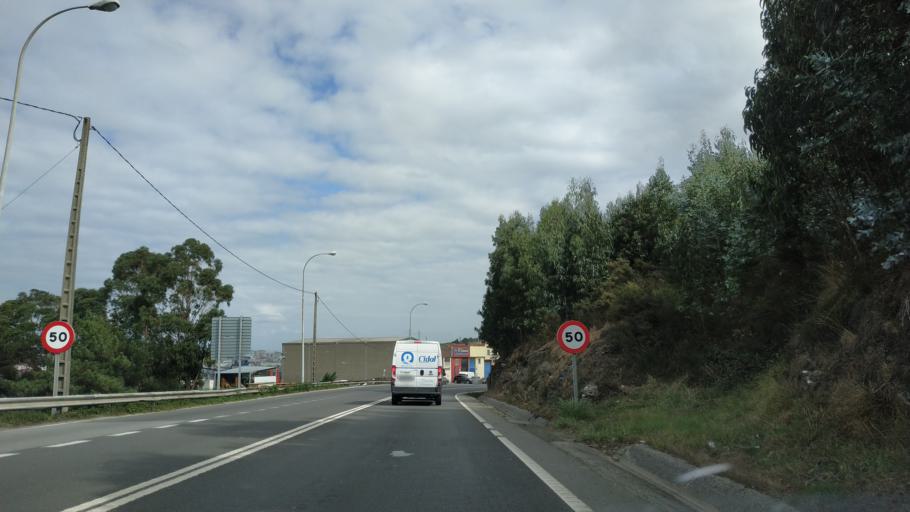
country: ES
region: Galicia
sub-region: Provincia da Coruna
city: A Coruna
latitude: 43.3392
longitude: -8.4502
